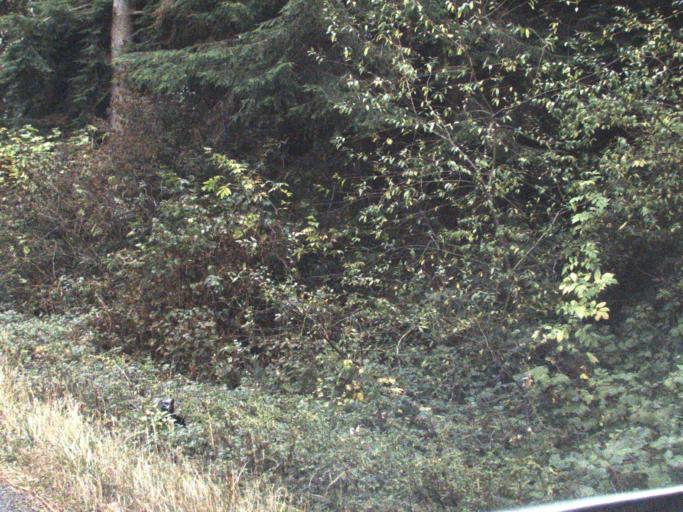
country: US
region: Washington
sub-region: Island County
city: Coupeville
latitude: 48.1761
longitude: -122.6171
